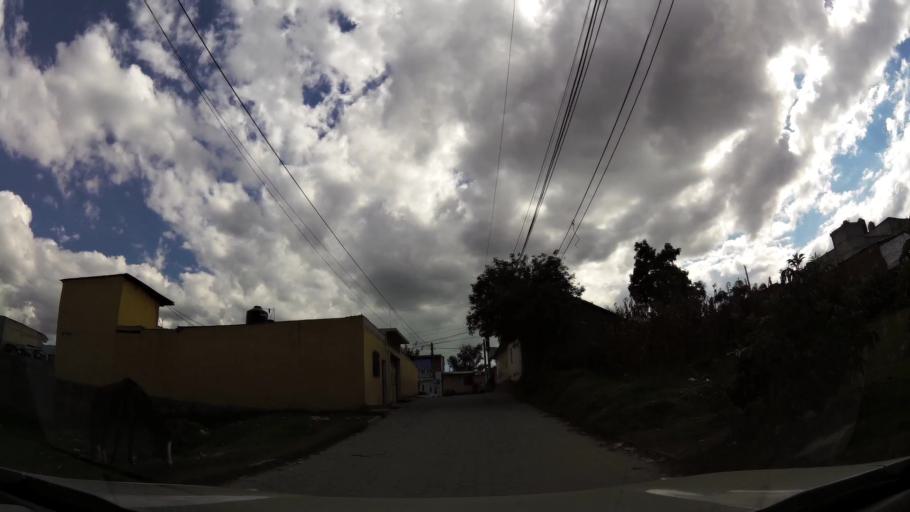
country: GT
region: Quetzaltenango
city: Quetzaltenango
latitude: 14.8368
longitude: -91.5421
